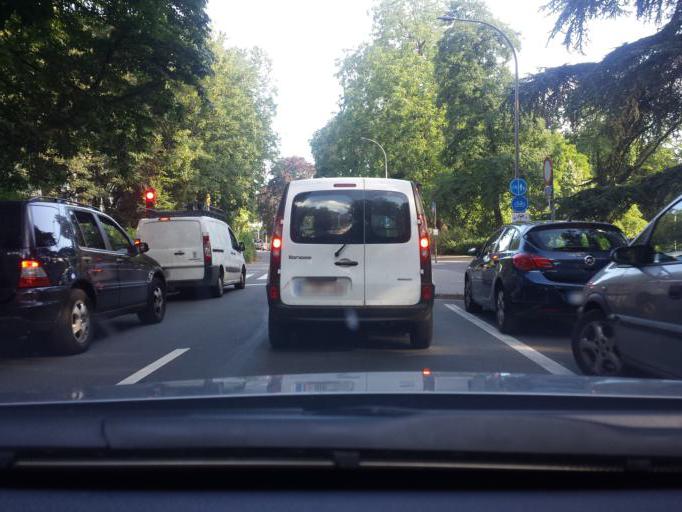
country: BE
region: Flanders
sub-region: Provincie Antwerpen
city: Antwerpen
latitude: 51.2135
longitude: 4.4159
